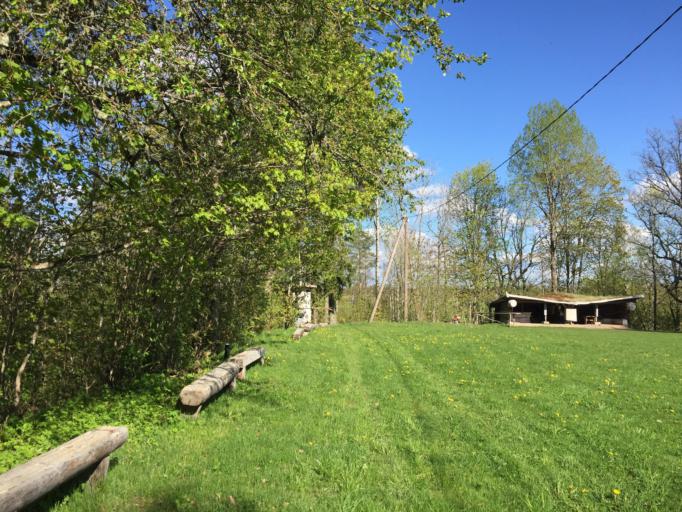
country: LV
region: Madonas Rajons
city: Madona
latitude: 56.8107
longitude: 26.0958
